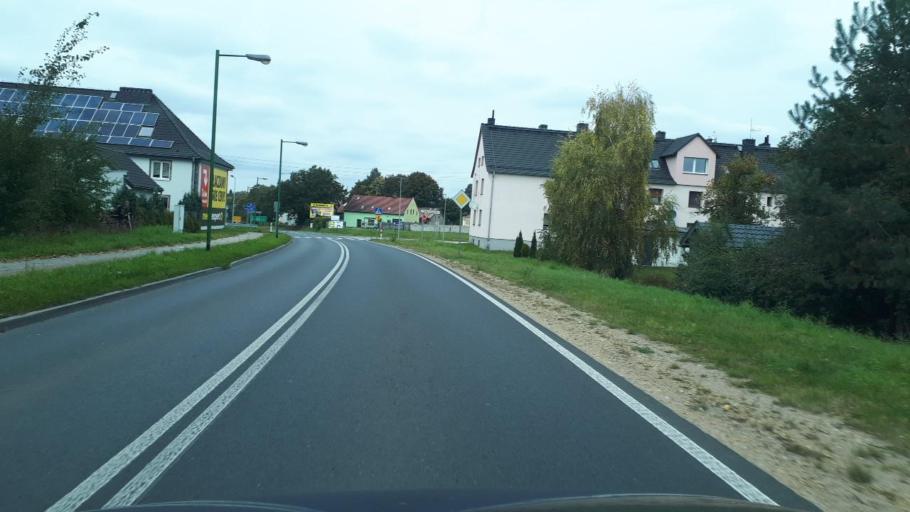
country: PL
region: Opole Voivodeship
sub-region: Powiat oleski
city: Olesno
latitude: 50.8722
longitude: 18.4173
